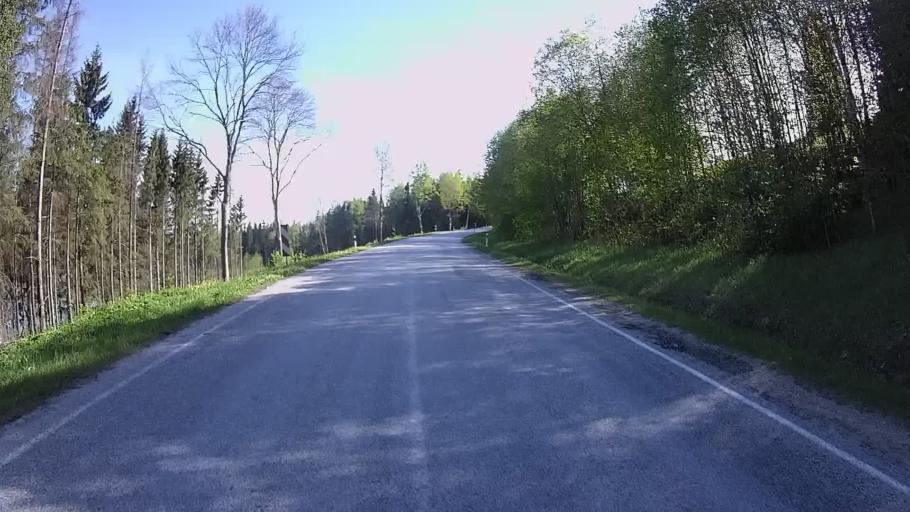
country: EE
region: Vorumaa
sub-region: Antsla vald
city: Vana-Antsla
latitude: 58.0177
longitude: 26.5000
